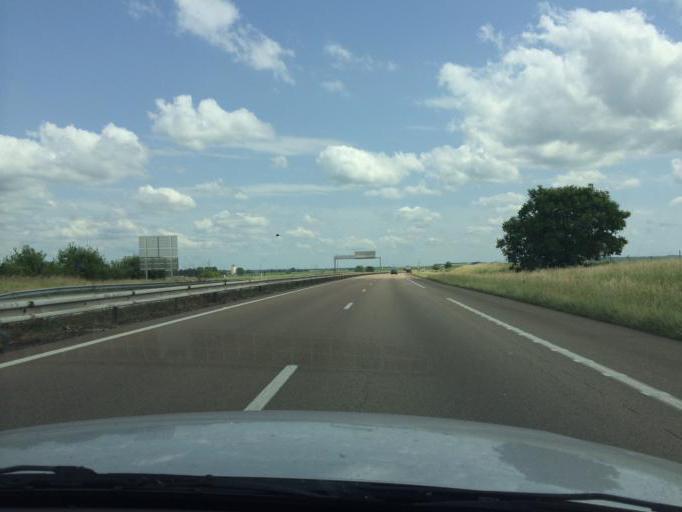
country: FR
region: Champagne-Ardenne
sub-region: Departement de la Marne
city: Verzy
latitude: 49.1692
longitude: 4.1787
